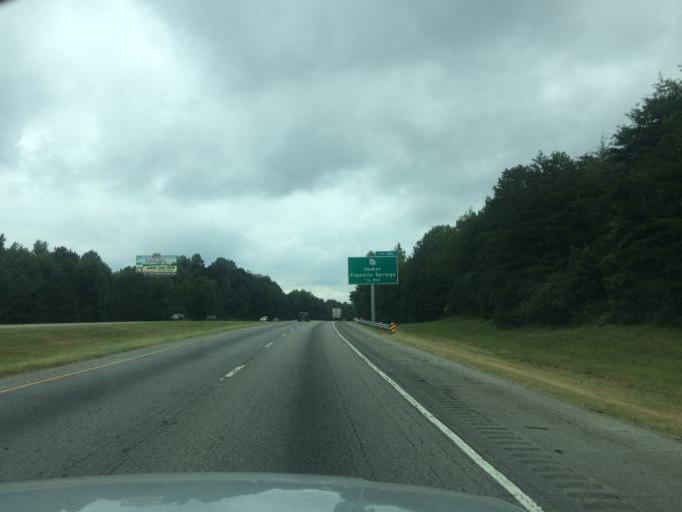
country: US
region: Georgia
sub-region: Franklin County
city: Carnesville
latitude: 34.3517
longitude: -83.3070
